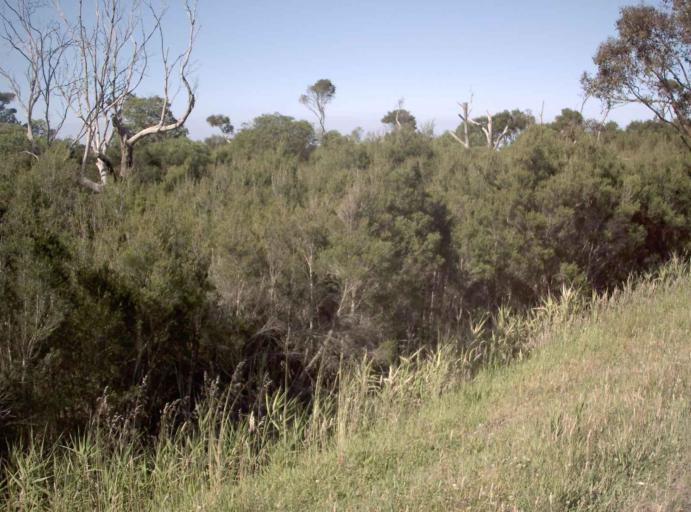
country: AU
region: Victoria
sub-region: Latrobe
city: Traralgon
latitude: -38.6223
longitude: 146.6636
